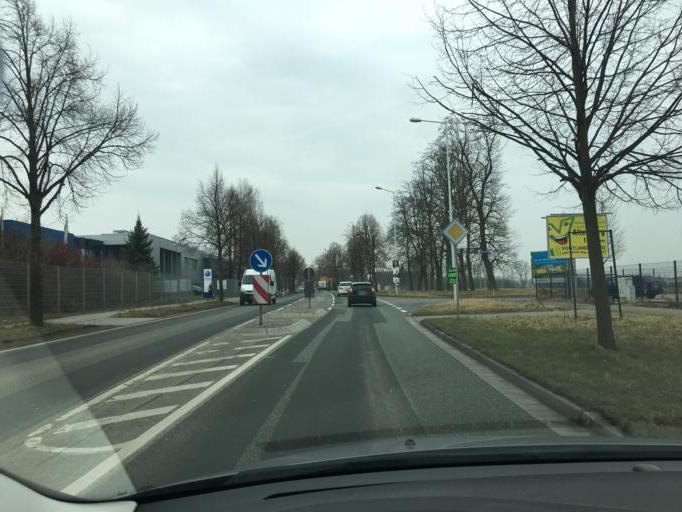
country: DE
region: Thuringia
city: Altenburg
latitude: 51.0063
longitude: 12.4523
